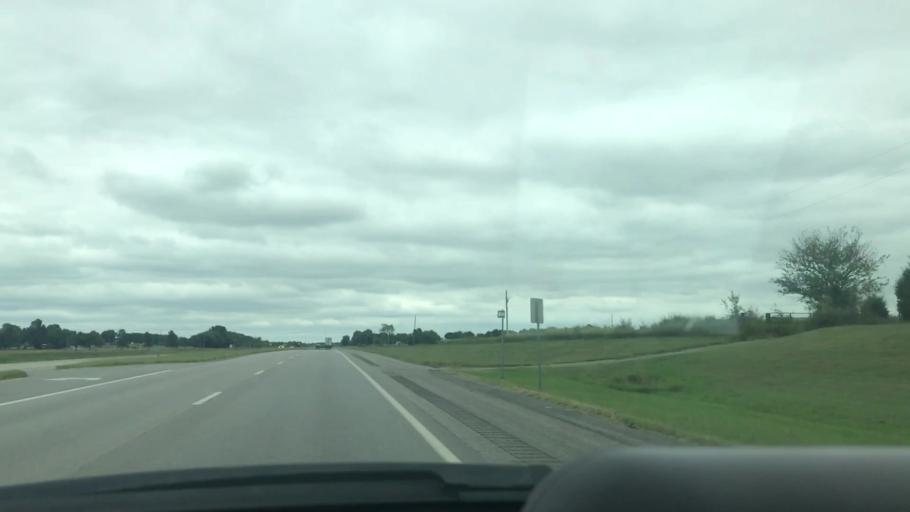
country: US
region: Oklahoma
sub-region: Mayes County
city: Pryor
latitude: 36.3305
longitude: -95.3100
